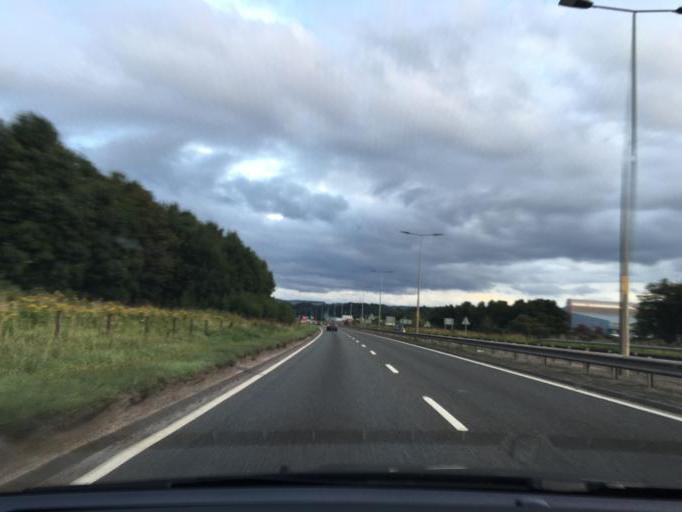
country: GB
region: Scotland
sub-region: Highland
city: Inverness
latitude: 57.4895
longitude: -4.2114
